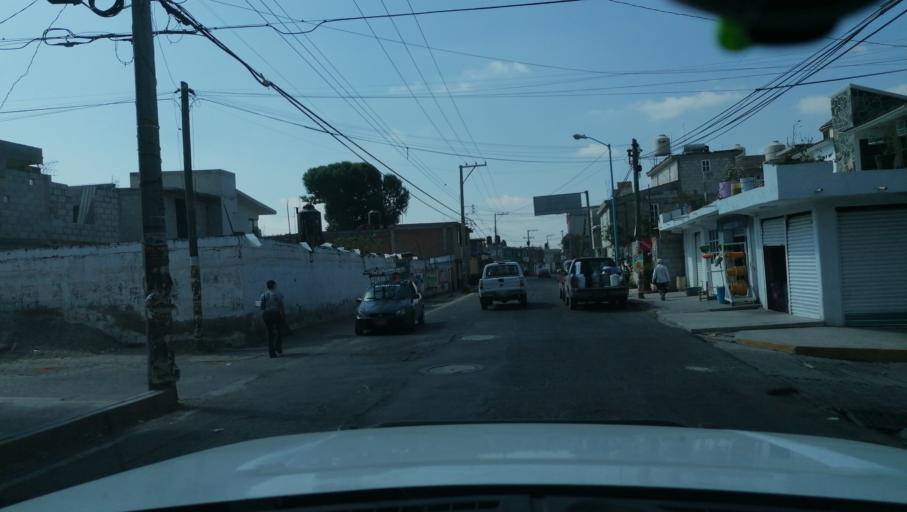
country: MX
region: Tlaxcala
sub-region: Tetlatlahuca
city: Tetlatlahuca
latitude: 19.2380
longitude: -98.3001
